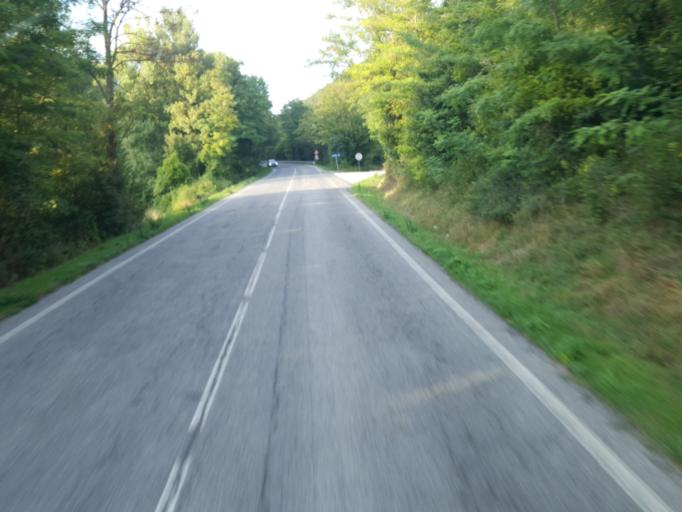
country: IT
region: The Marches
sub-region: Provincia di Ancona
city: Fabriano
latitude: 43.3191
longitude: 12.8384
